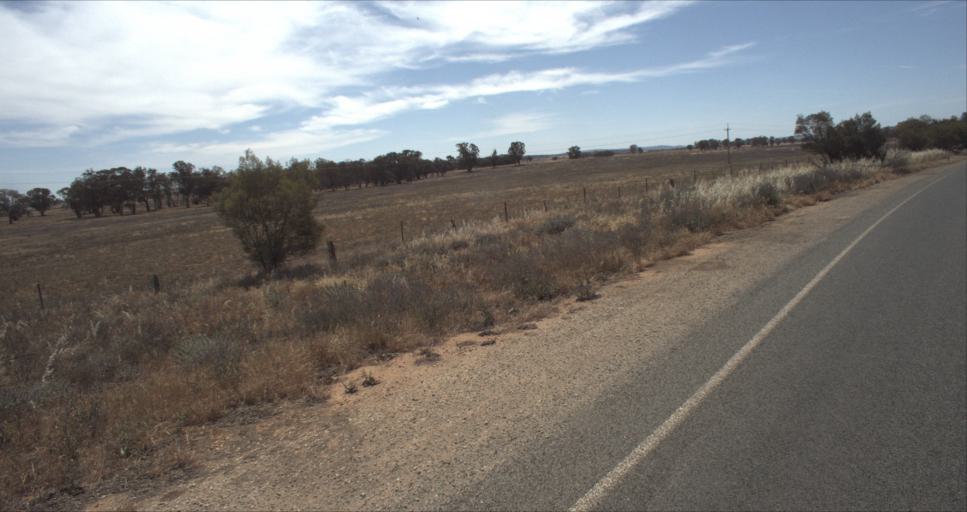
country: AU
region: New South Wales
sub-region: Leeton
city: Leeton
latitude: -34.6623
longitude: 146.4498
